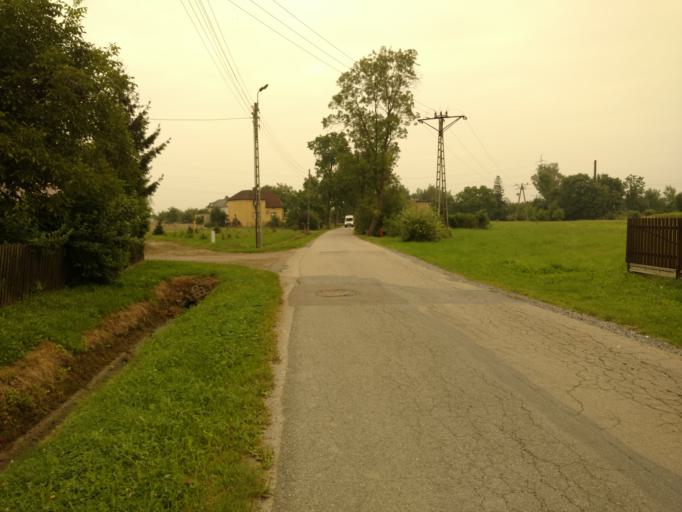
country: PL
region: Silesian Voivodeship
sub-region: Powiat pszczynski
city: Pszczyna
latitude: 49.9939
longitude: 18.9586
